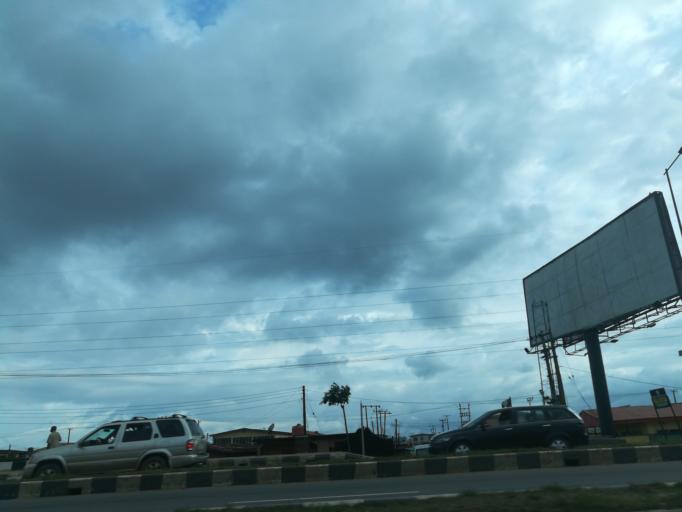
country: NG
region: Lagos
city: Ojota
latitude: 6.6089
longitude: 3.4251
